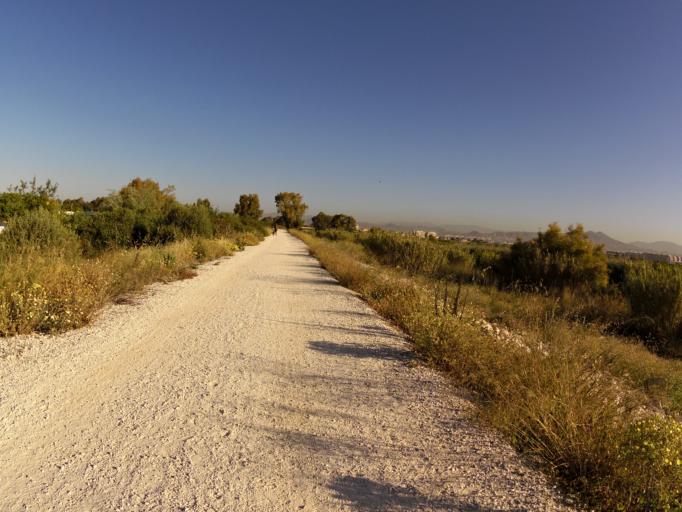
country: ES
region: Andalusia
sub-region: Provincia de Malaga
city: Torremolinos
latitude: 36.6690
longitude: -4.4590
